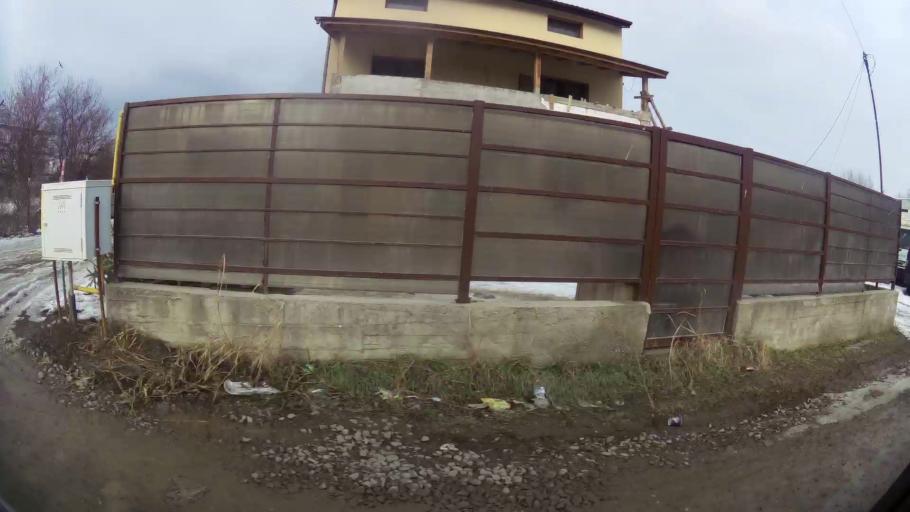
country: RO
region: Ilfov
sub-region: Comuna Popesti-Leordeni
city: Popesti-Leordeni
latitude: 44.4010
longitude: 26.1754
